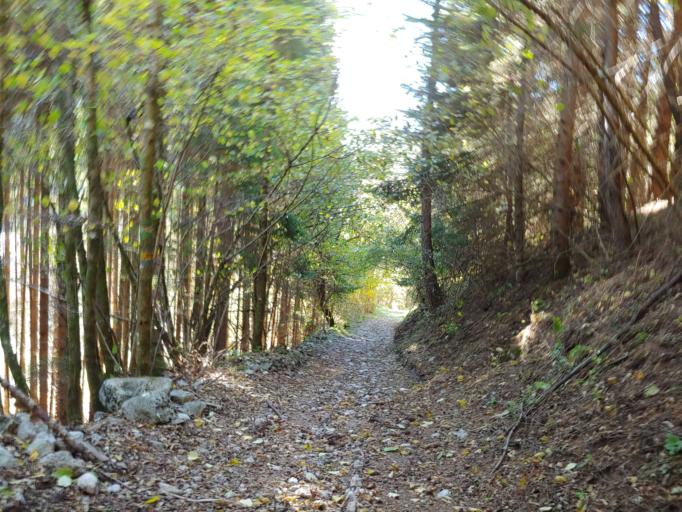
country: IT
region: Veneto
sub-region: Provincia di Belluno
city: Lozzo di Cadore
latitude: 46.4903
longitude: 12.4414
